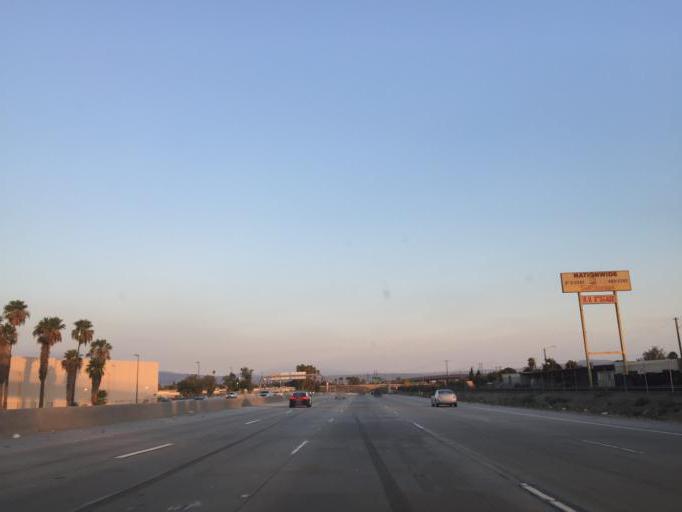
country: US
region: California
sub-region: San Bernardino County
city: San Bernardino
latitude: 34.1330
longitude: -117.3085
